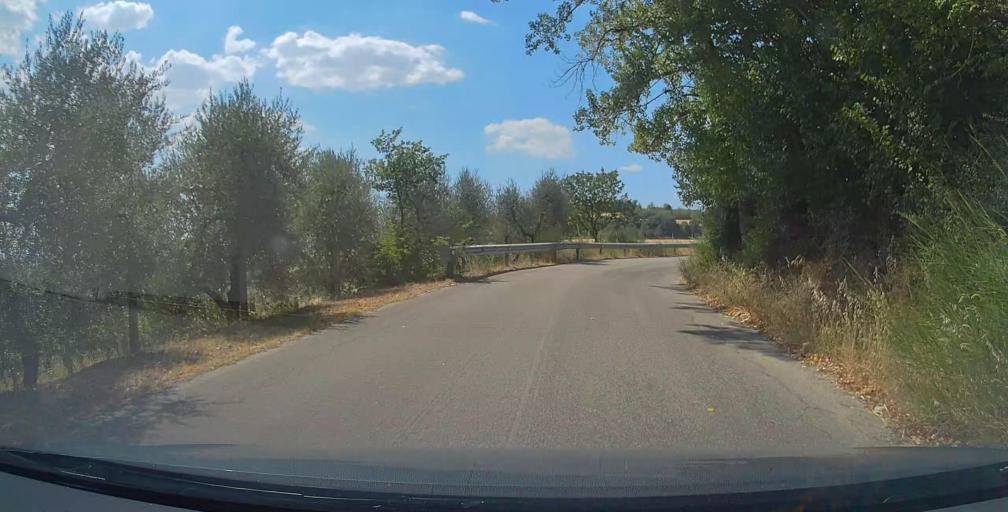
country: IT
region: Umbria
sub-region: Provincia di Terni
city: Otricoli
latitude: 42.4010
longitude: 12.4915
